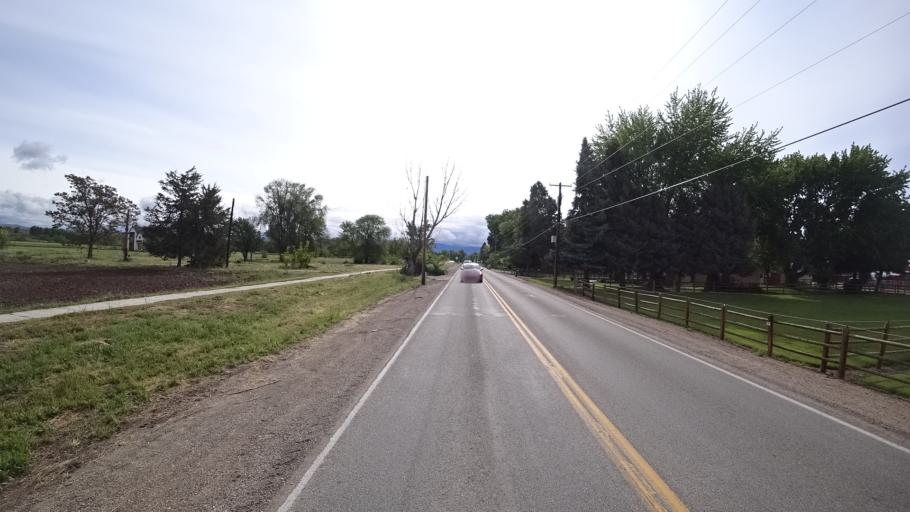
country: US
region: Idaho
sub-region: Ada County
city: Eagle
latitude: 43.7208
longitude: -116.3789
